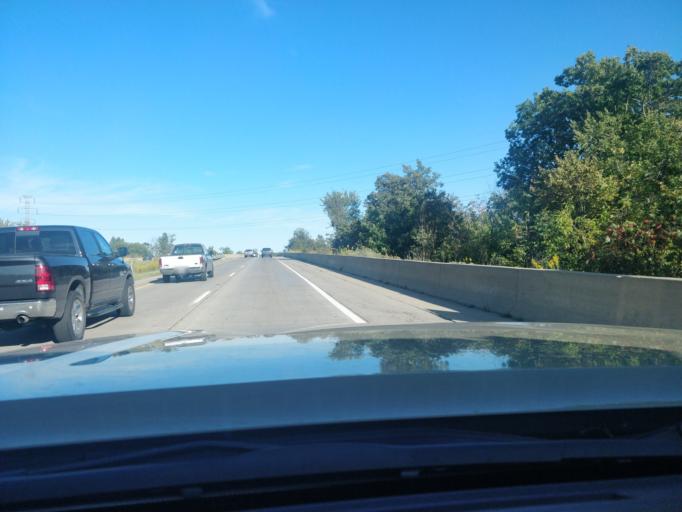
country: US
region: Michigan
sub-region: Wayne County
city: Taylor
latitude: 42.1902
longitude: -83.2564
